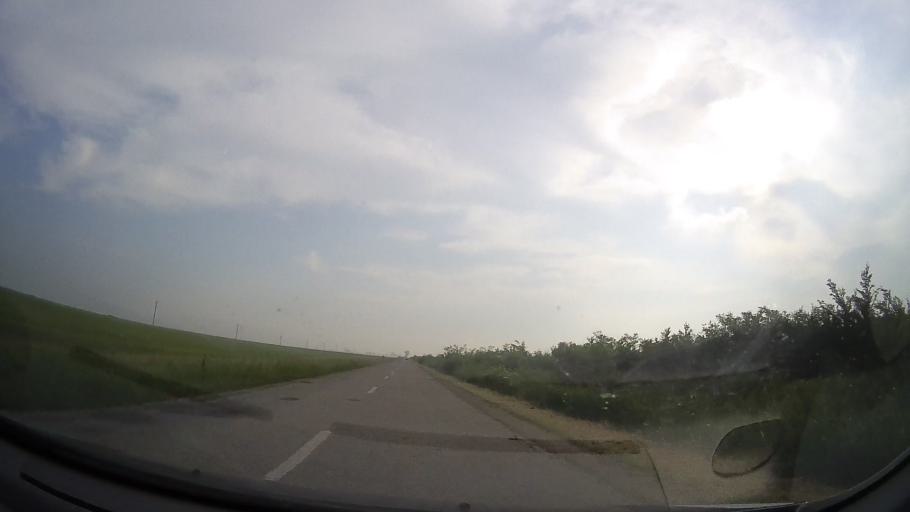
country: RO
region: Timis
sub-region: Comuna Giulvaz
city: Giulvaz
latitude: 45.5749
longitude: 21.0149
